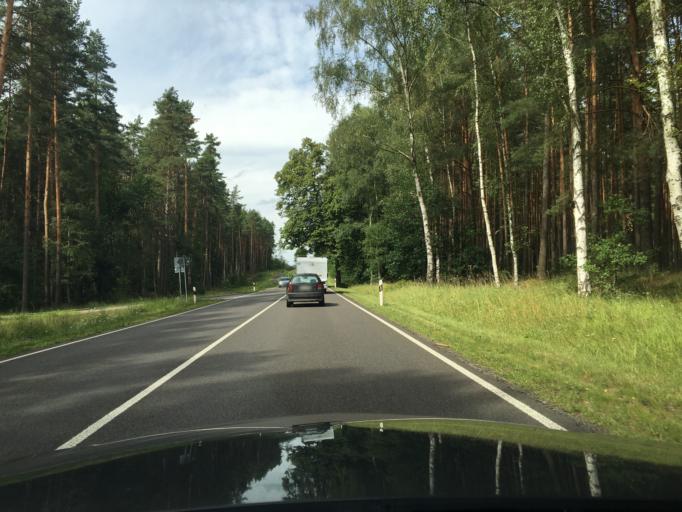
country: DE
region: Mecklenburg-Vorpommern
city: Neustrelitz
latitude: 53.2984
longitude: 13.1062
